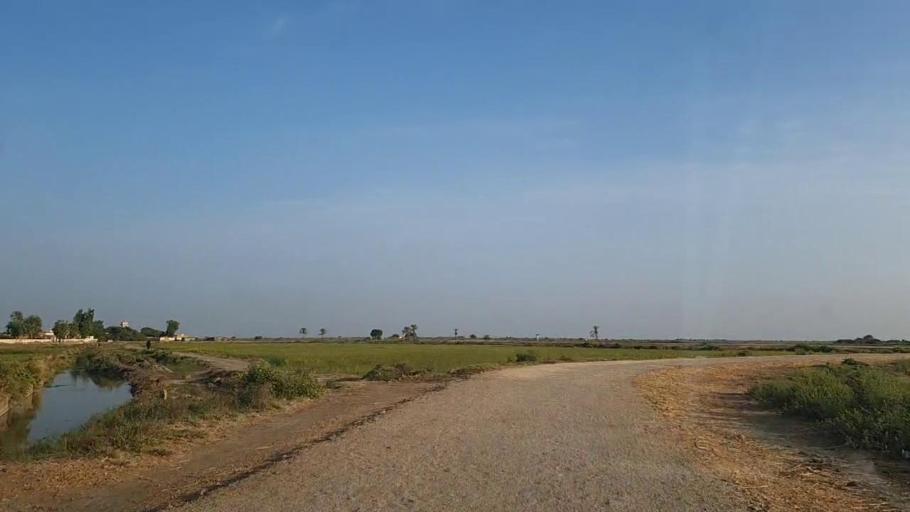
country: PK
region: Sindh
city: Mirpur Batoro
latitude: 24.6083
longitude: 68.0947
